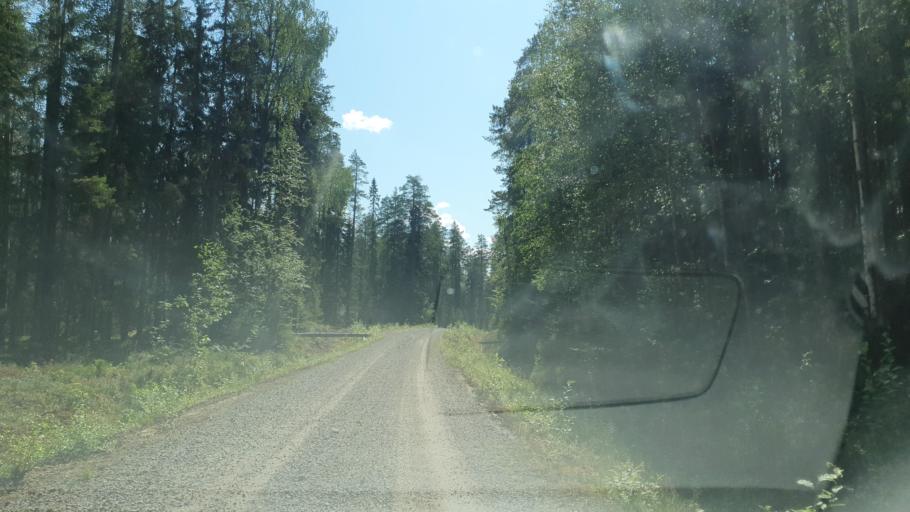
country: FI
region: Kainuu
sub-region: Kehys-Kainuu
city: Kuhmo
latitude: 63.9780
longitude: 29.5435
